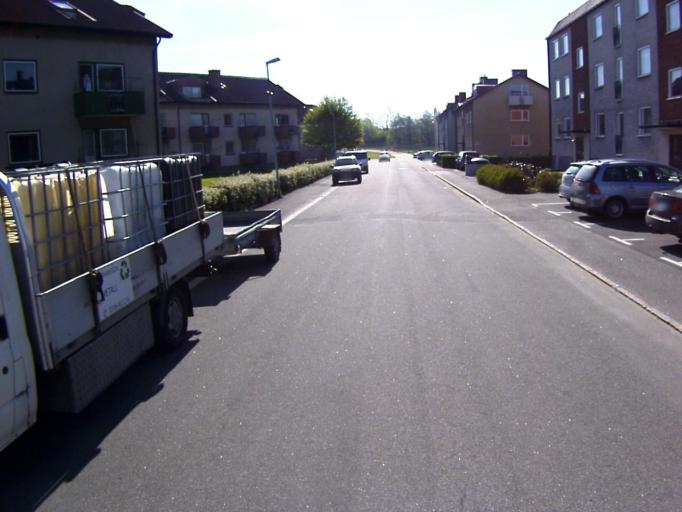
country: SE
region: Skane
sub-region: Kristianstads Kommun
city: Onnestad
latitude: 55.9312
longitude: 13.9789
